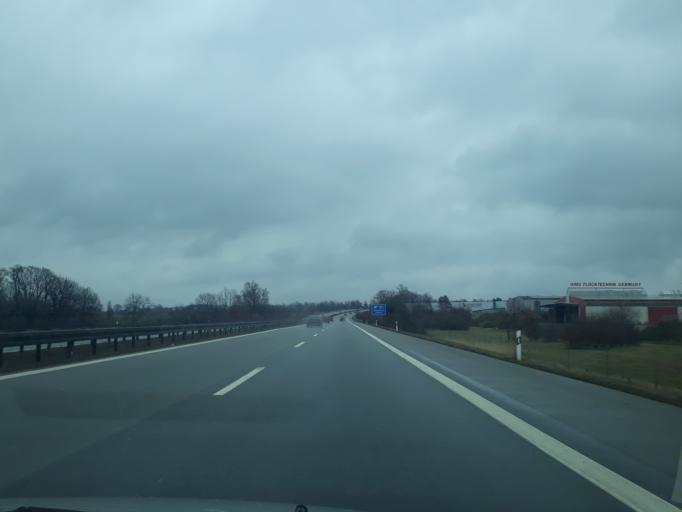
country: DE
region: Saxony
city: Goda
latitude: 51.1974
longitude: 14.3388
